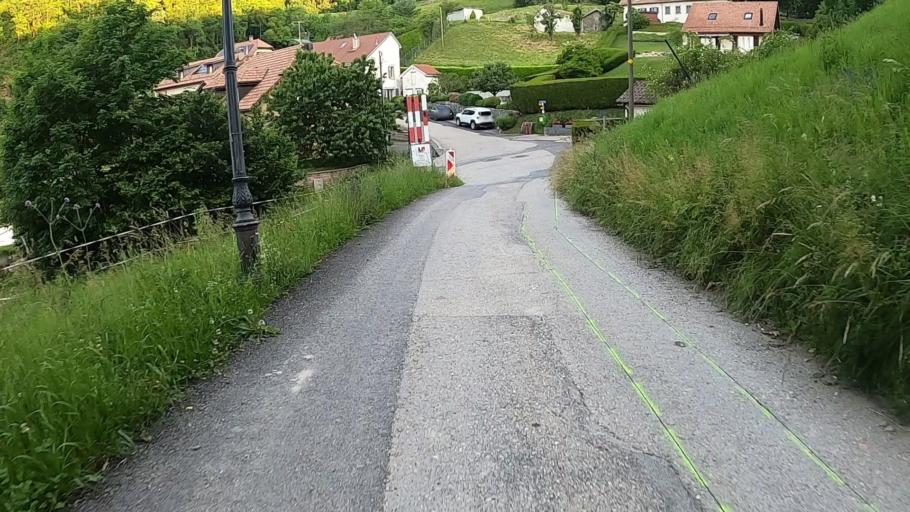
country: CH
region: Vaud
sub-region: Nyon District
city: Rolle
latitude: 46.4770
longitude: 6.3310
